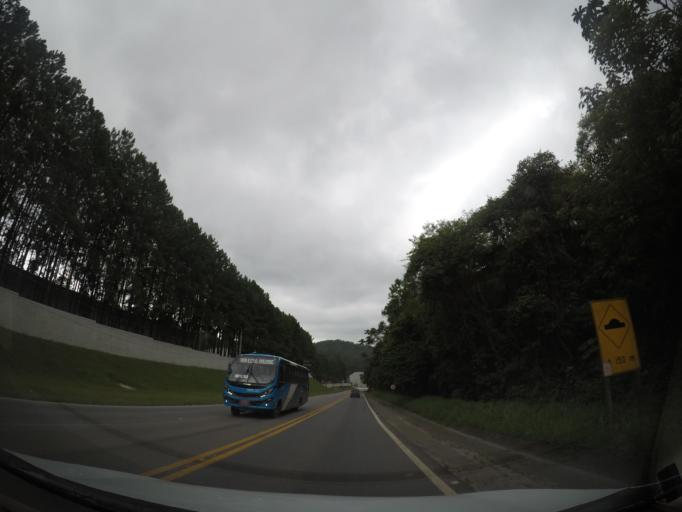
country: BR
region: Sao Paulo
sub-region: Aruja
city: Aruja
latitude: -23.3614
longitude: -46.4241
